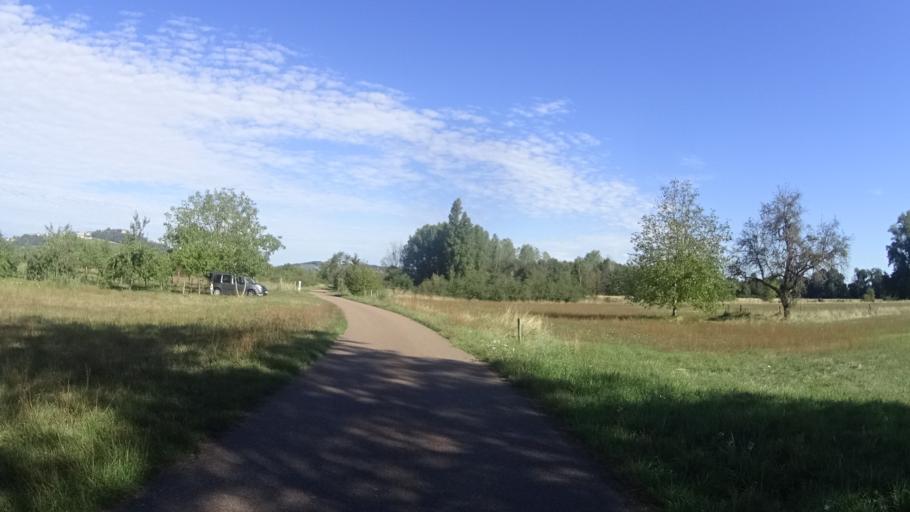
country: FR
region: Centre
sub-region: Departement du Cher
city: Sancerre
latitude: 47.3192
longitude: 2.8701
